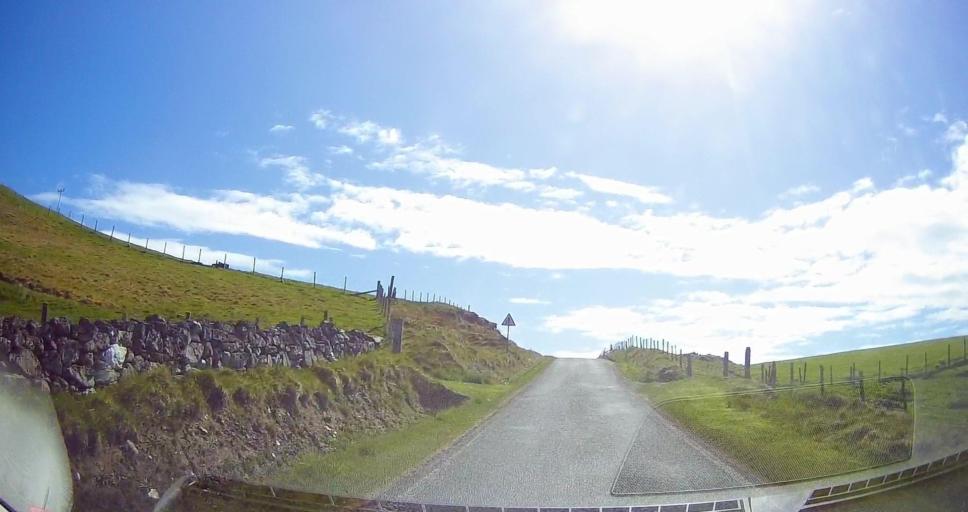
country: GB
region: Scotland
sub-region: Shetland Islands
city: Sandwick
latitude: 59.9620
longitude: -1.3231
